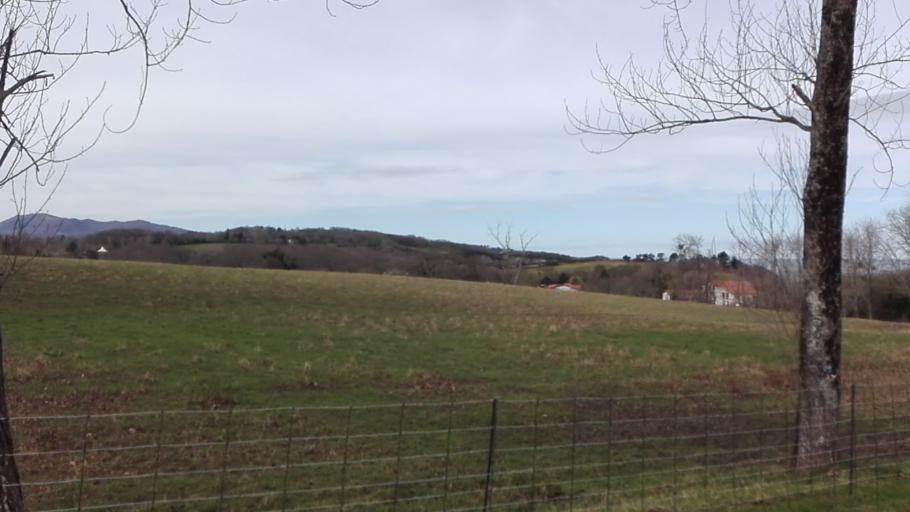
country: FR
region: Aquitaine
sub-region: Departement des Pyrenees-Atlantiques
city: Urrugne
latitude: 43.3780
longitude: -1.7296
